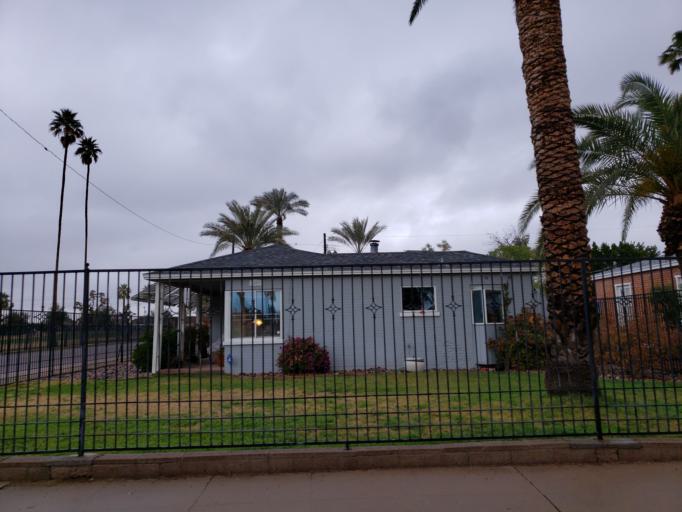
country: US
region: Arizona
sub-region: Maricopa County
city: Phoenix
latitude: 33.4787
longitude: -112.0936
